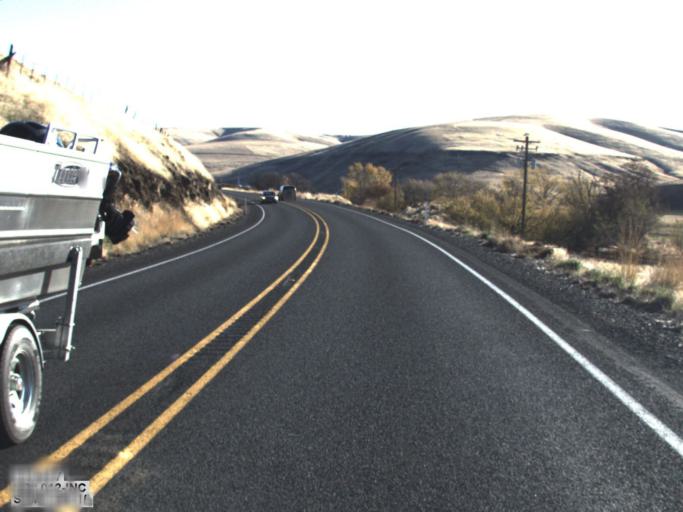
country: US
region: Washington
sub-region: Garfield County
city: Pomeroy
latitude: 46.4643
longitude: -117.7037
